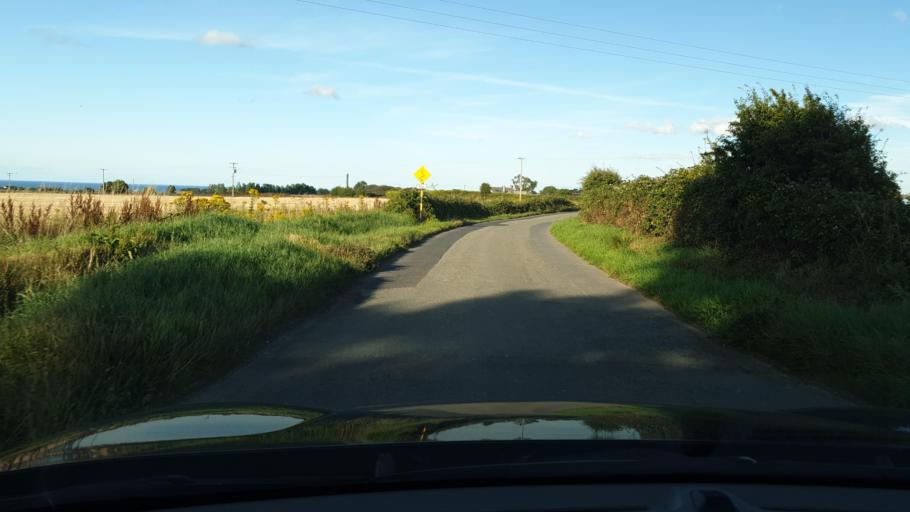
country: IE
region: Leinster
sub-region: Fingal County
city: Skerries
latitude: 53.5579
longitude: -6.1284
